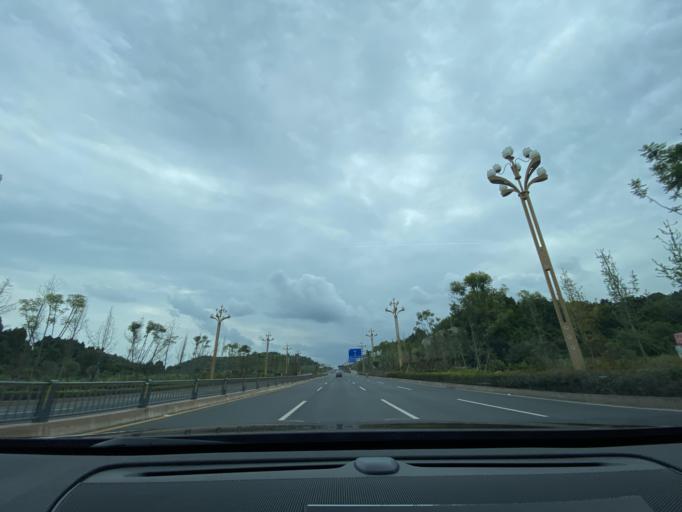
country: CN
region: Sichuan
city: Jiancheng
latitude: 30.4580
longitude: 104.4958
